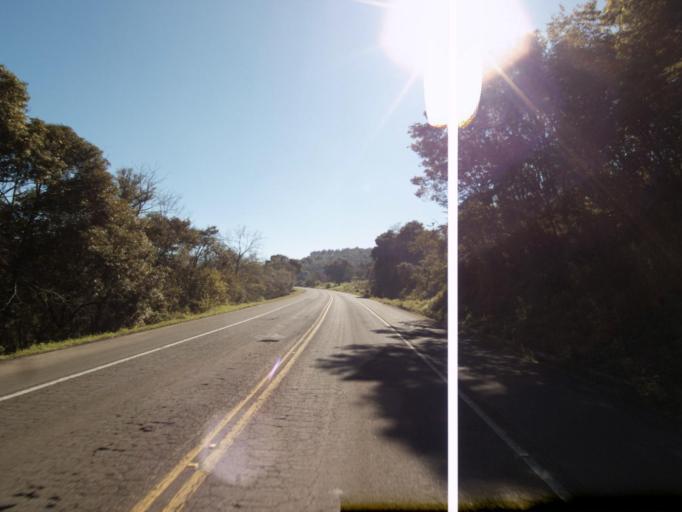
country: BR
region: Rio Grande do Sul
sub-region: Frederico Westphalen
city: Frederico Westphalen
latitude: -27.0100
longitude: -53.2247
